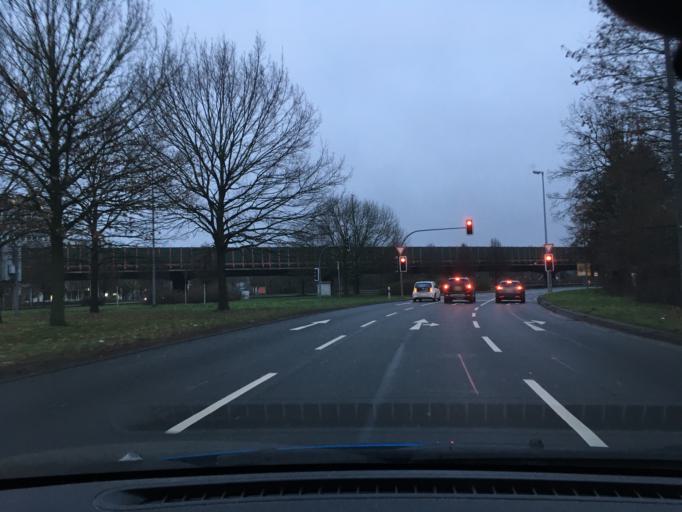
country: DE
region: Lower Saxony
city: Hannover
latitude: 52.3952
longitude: 9.7929
